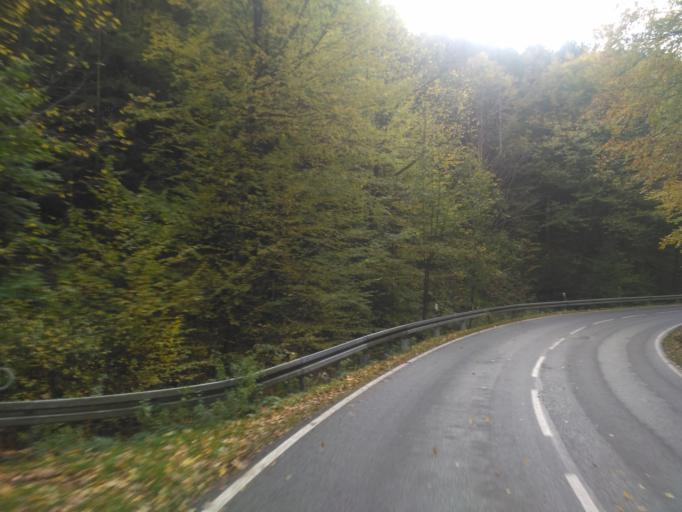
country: DE
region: Saxony
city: Sebnitz
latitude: 50.9621
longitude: 14.2232
